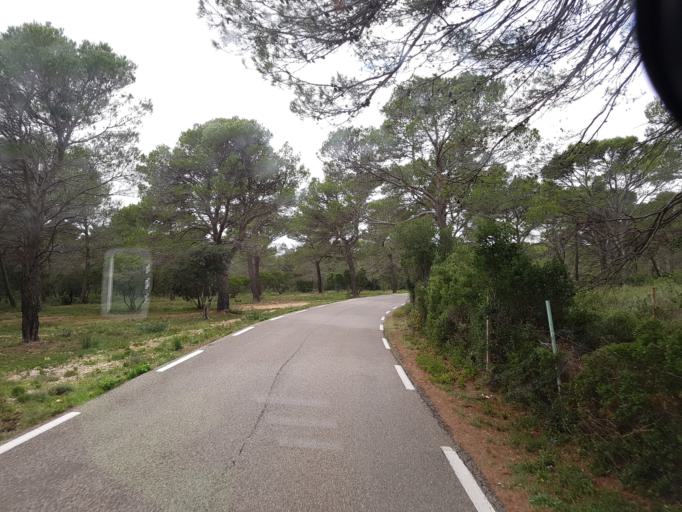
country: FR
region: Provence-Alpes-Cote d'Azur
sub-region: Departement des Bouches-du-Rhone
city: Cuges-les-Pins
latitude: 43.2508
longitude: 5.7333
